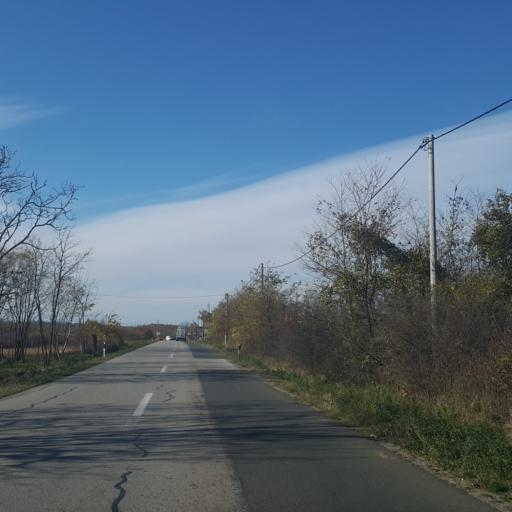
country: RS
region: Central Serbia
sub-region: Sumadijski Okrug
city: Topola
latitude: 44.2519
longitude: 20.7591
